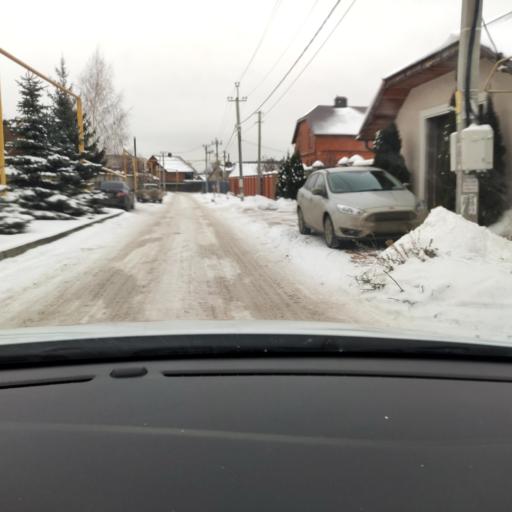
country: RU
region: Tatarstan
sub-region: Gorod Kazan'
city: Kazan
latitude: 55.7886
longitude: 49.2372
